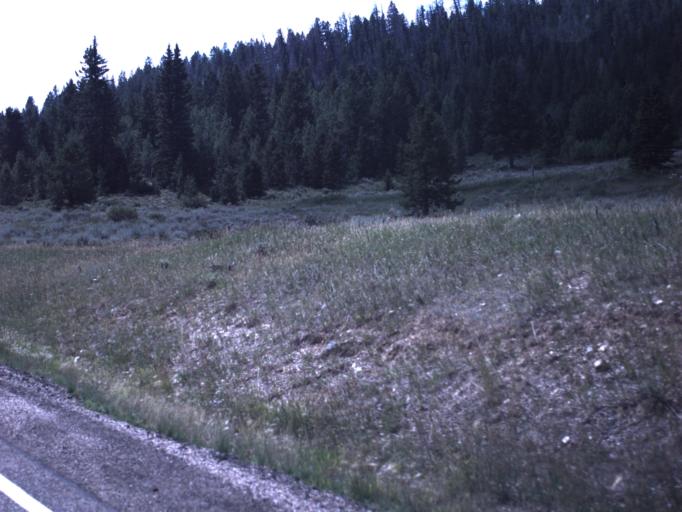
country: US
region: Utah
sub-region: Uintah County
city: Maeser
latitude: 40.7051
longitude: -109.4937
